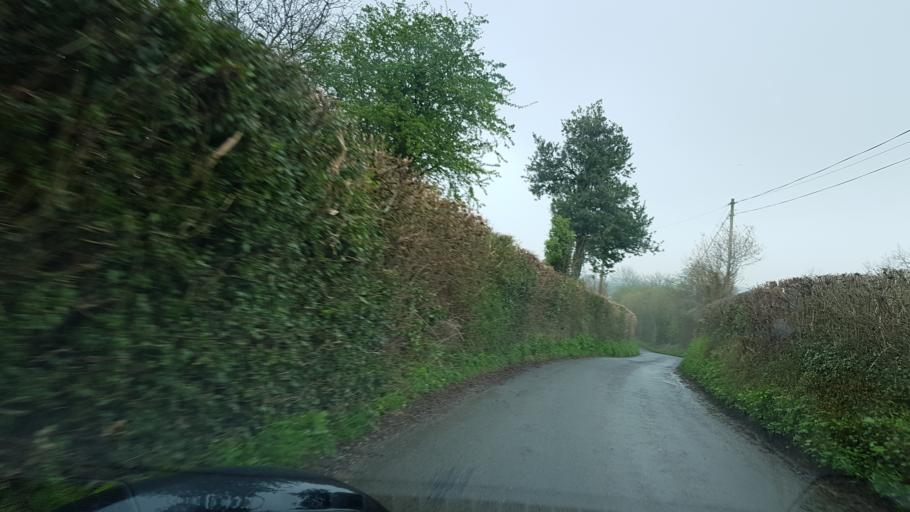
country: GB
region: England
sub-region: Herefordshire
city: Yatton
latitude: 52.0001
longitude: -2.5130
